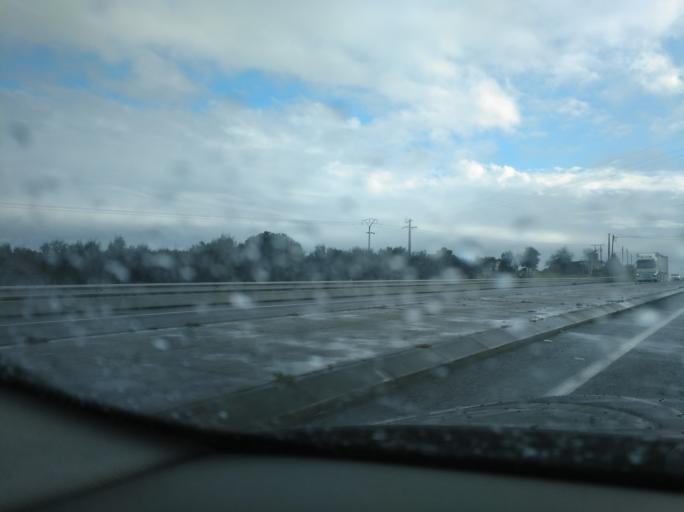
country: PT
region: Setubal
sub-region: Grandola
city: Grandola
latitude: 38.0748
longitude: -8.4165
